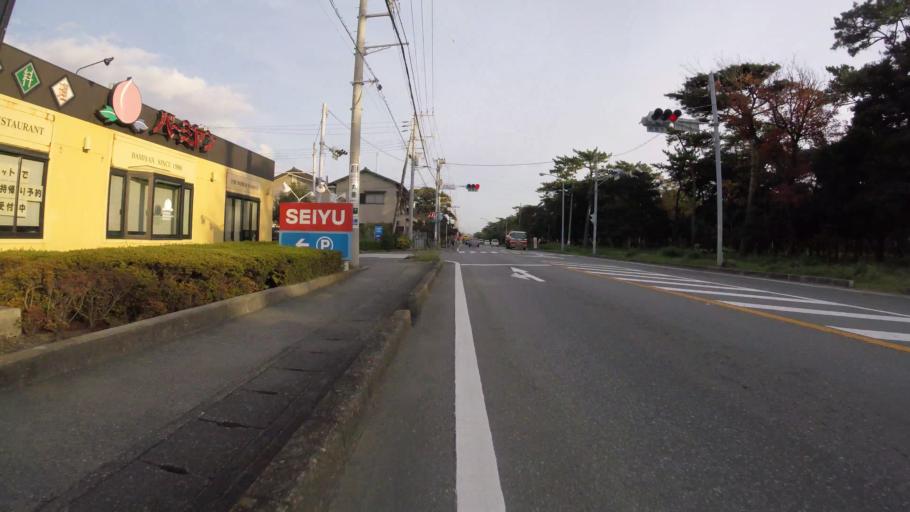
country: JP
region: Shizuoka
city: Numazu
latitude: 35.1143
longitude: 138.8189
